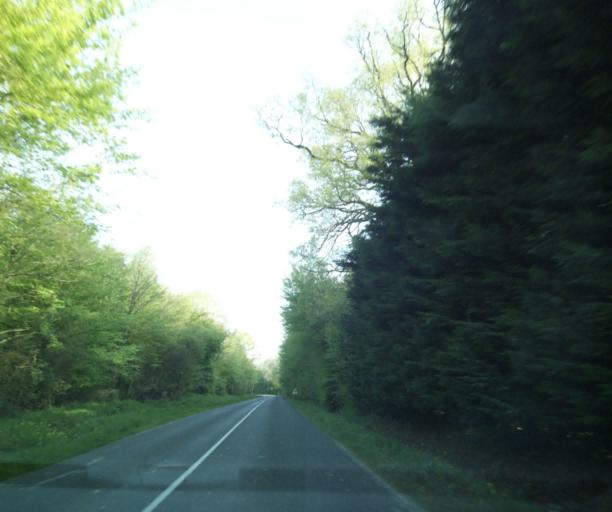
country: FR
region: Ile-de-France
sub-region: Departement de Seine-et-Marne
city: Vernou-la-Celle-sur-Seine
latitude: 48.4484
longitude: 2.8593
